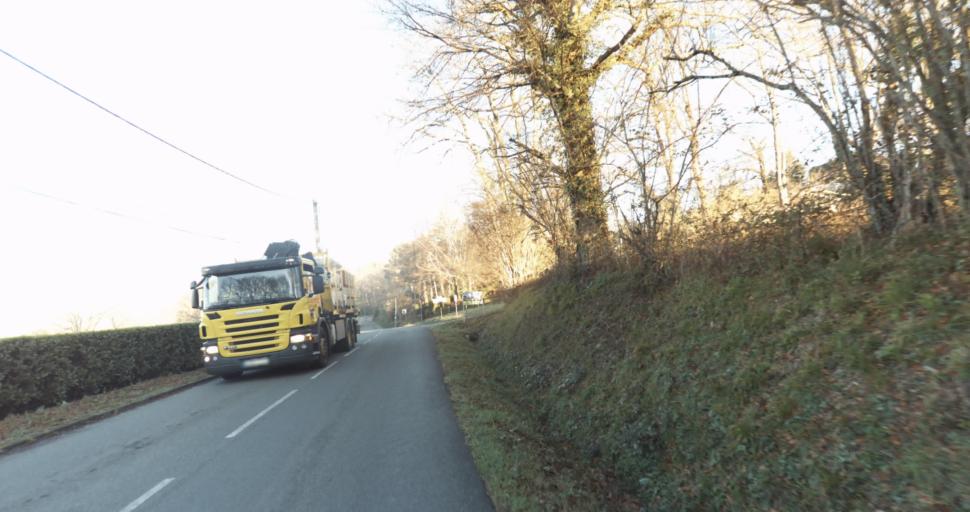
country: FR
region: Aquitaine
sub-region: Departement des Pyrenees-Atlantiques
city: Morlaas
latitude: 43.3287
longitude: -0.2692
